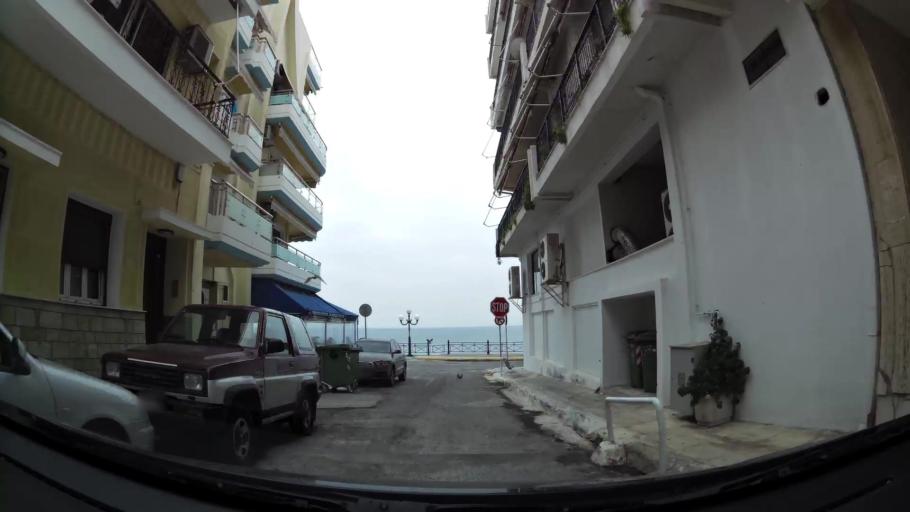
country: GR
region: Attica
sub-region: Nomos Attikis
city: Piraeus
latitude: 37.9292
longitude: 23.6288
